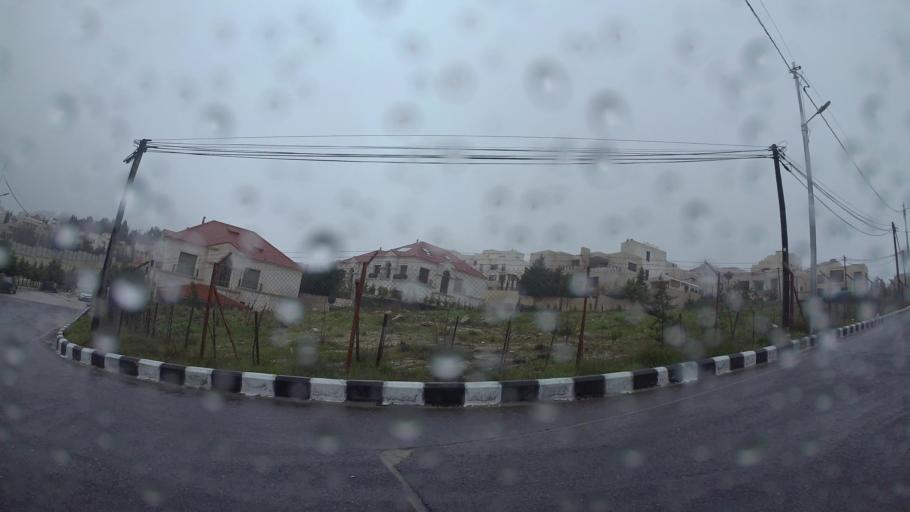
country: JO
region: Amman
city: Al Jubayhah
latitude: 32.0076
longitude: 35.8315
